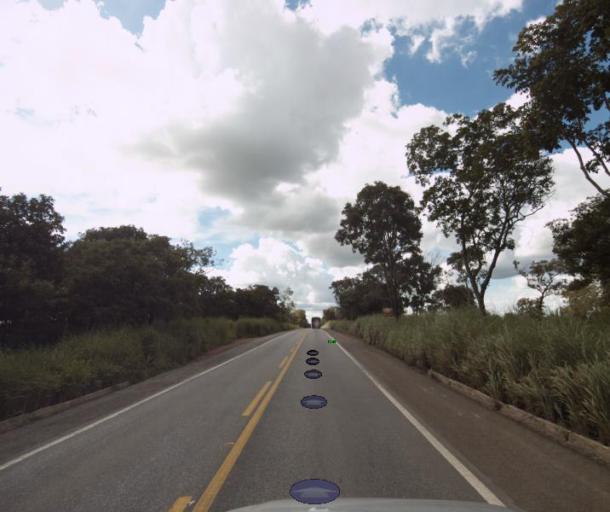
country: BR
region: Goias
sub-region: Porangatu
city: Porangatu
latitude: -13.2990
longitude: -49.1218
